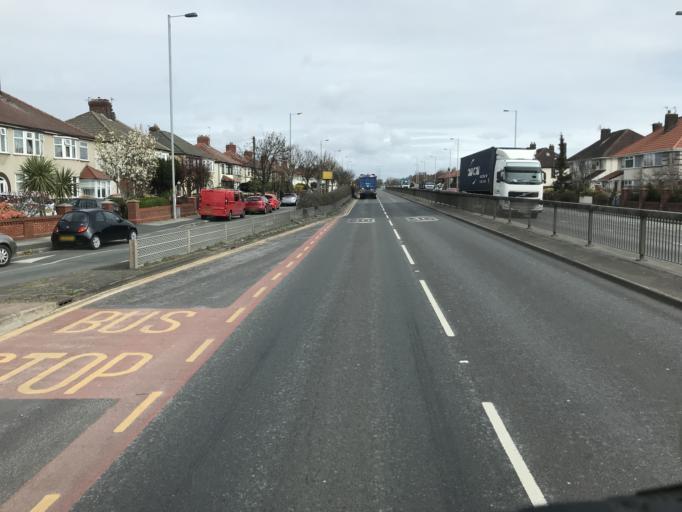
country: GB
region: England
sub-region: Sefton
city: Litherland
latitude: 53.4724
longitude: -2.9907
